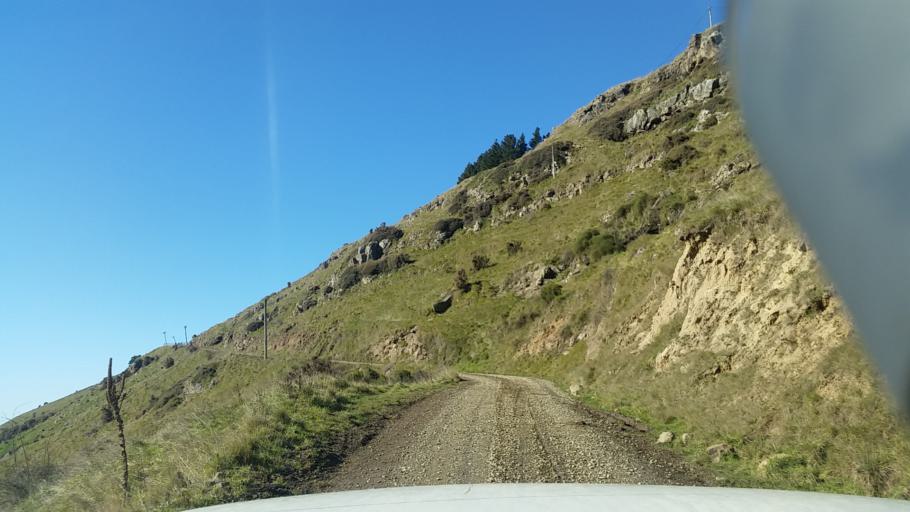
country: NZ
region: Canterbury
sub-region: Christchurch City
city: Christchurch
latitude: -43.6630
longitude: 172.9891
